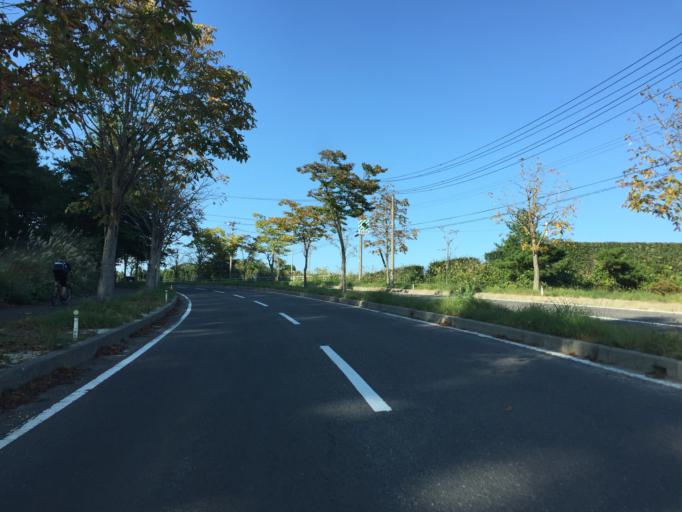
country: JP
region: Fukushima
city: Fukushima-shi
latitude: 37.6873
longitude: 140.4760
